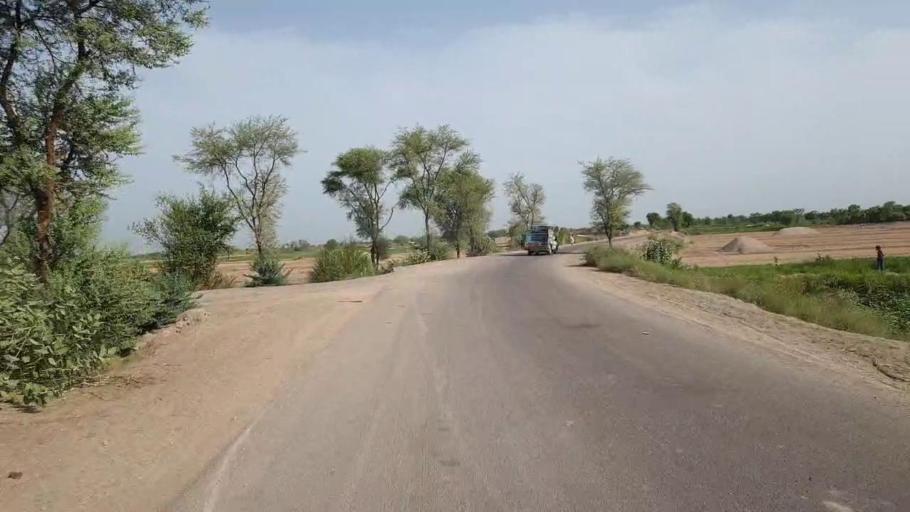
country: PK
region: Sindh
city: Sakrand
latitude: 26.2612
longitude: 68.2847
